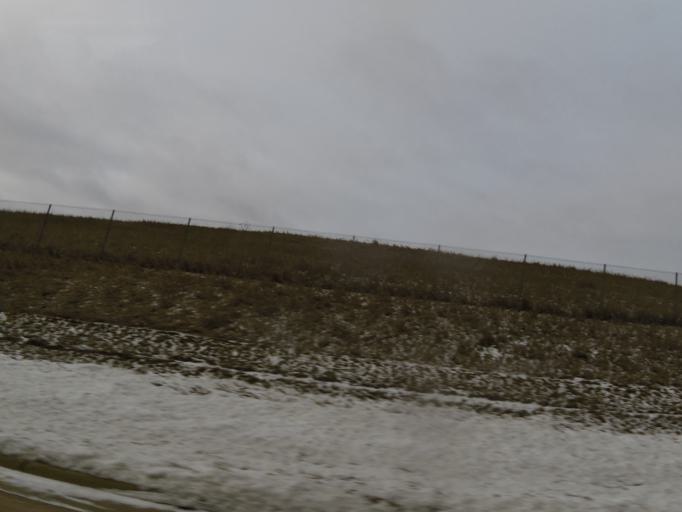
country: US
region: Minnesota
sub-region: Carver County
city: Carver
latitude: 44.7516
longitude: -93.6441
